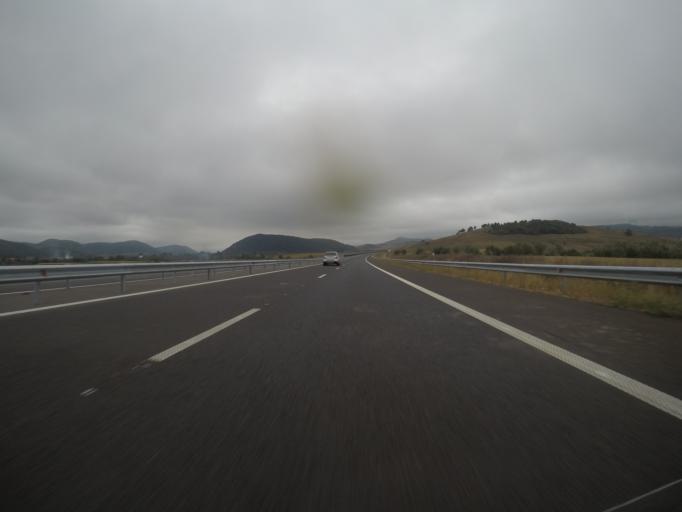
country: RO
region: Hunedoara
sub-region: Comuna Branisca
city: Branisca
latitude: 45.9253
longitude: 22.7742
